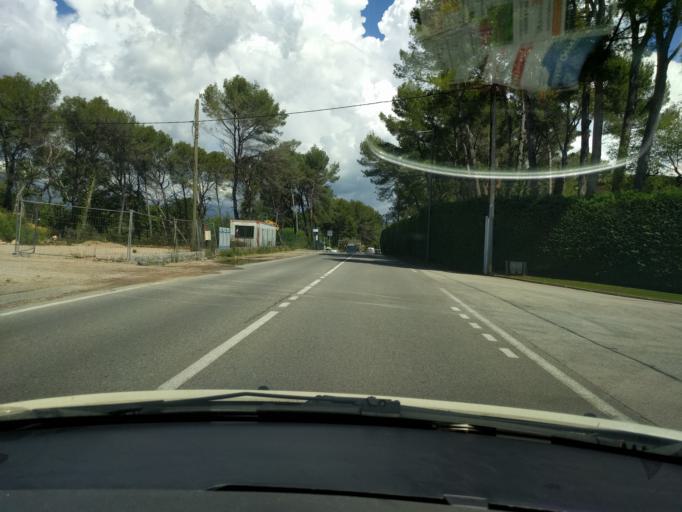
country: FR
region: Provence-Alpes-Cote d'Azur
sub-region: Departement des Alpes-Maritimes
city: La Roquette-sur-Siagne
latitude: 43.6033
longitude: 6.9599
